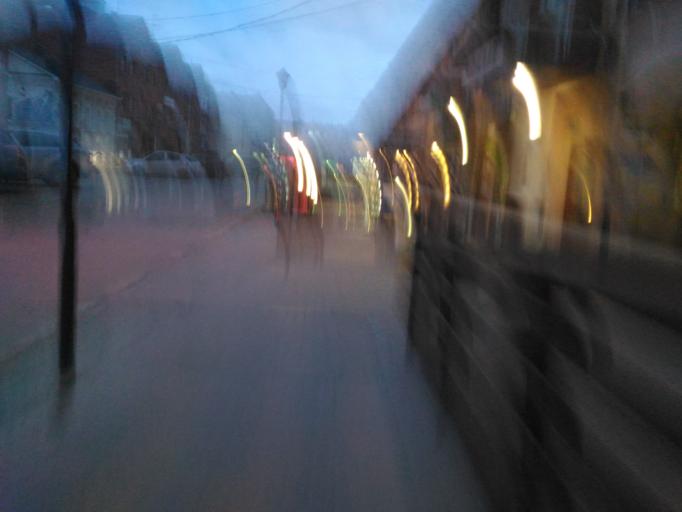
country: RU
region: Ulyanovsk
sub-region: Ulyanovskiy Rayon
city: Ulyanovsk
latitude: 54.3218
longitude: 48.3956
